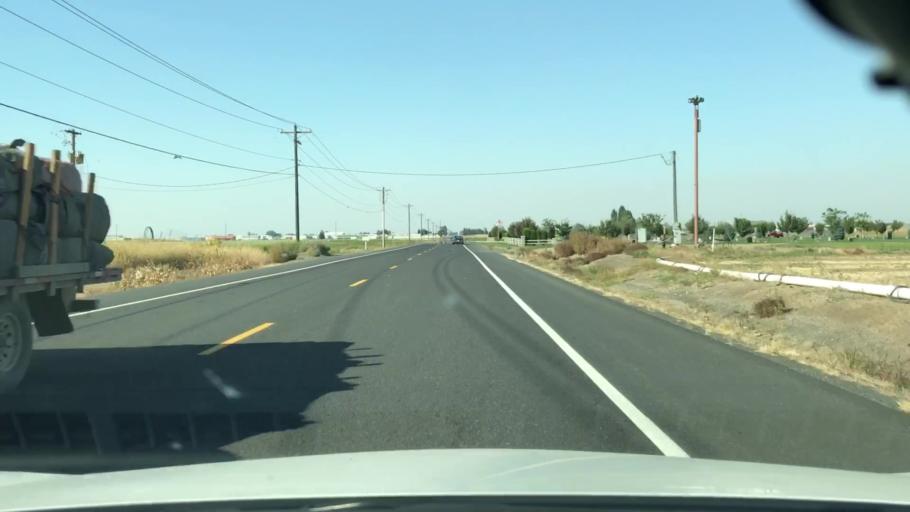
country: US
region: Washington
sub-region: Grant County
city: Moses Lake
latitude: 47.1231
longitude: -119.2358
